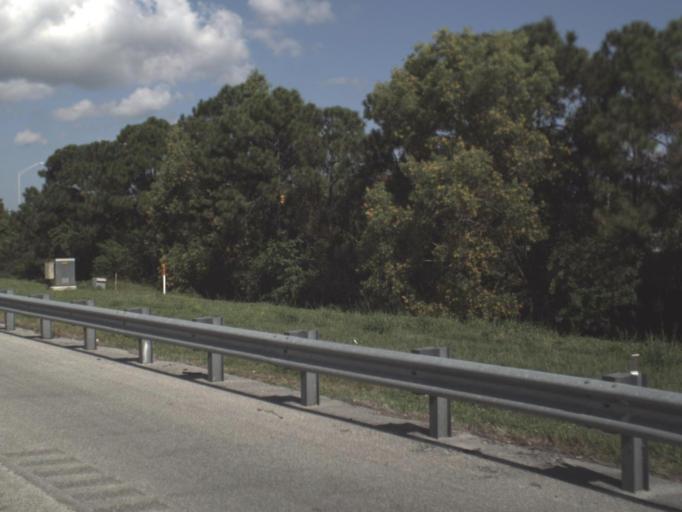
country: US
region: Florida
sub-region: Palm Beach County
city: Limestone Creek
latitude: 26.9155
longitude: -80.1452
